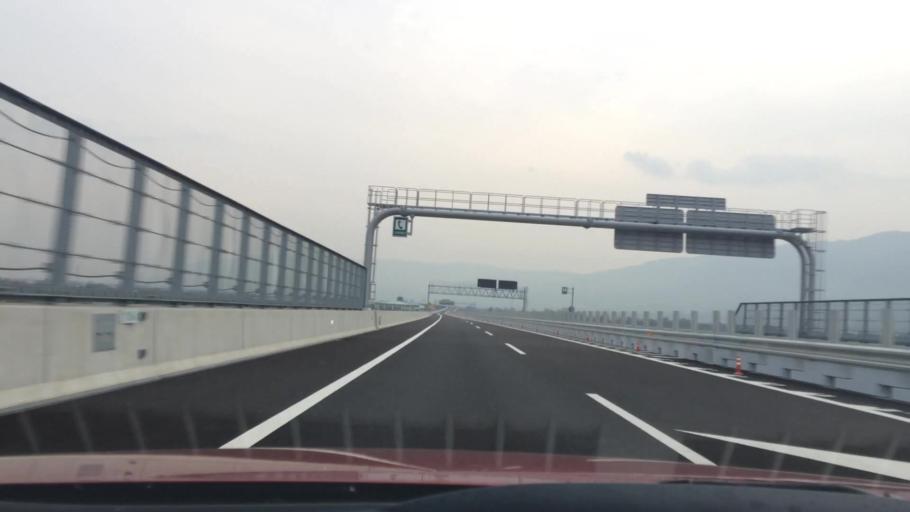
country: JP
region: Gifu
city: Ogaki
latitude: 35.3086
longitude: 136.5783
